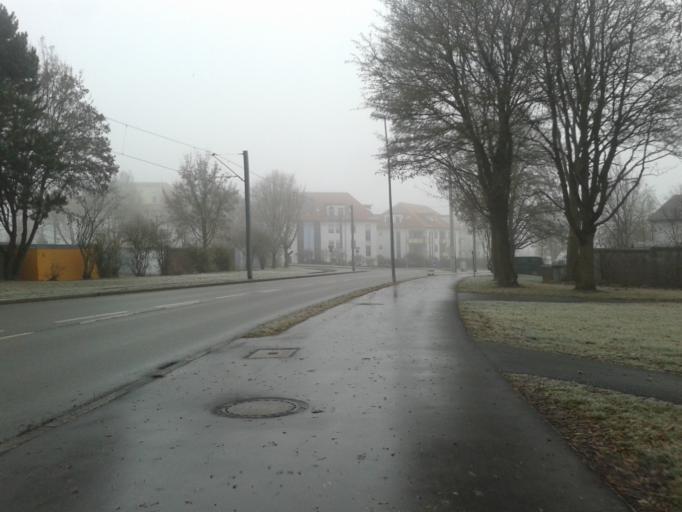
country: DE
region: Bavaria
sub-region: Swabia
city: Neu-Ulm
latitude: 48.4341
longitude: 10.0303
